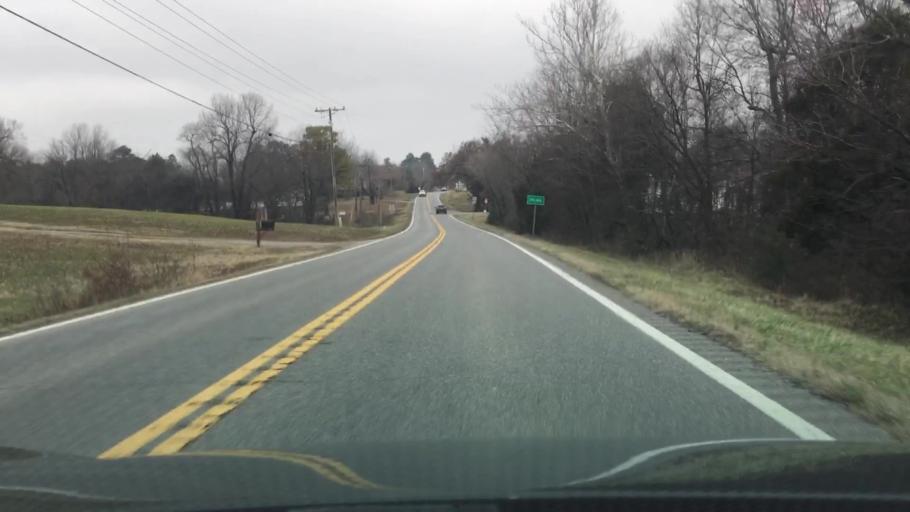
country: US
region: Kentucky
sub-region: Marshall County
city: Calvert City
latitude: 36.9566
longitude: -88.3728
